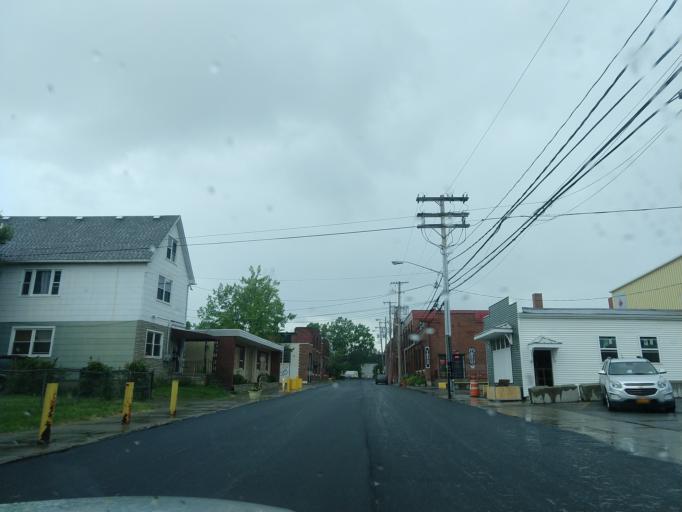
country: US
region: New York
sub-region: Erie County
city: Kenmore
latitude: 42.9422
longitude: -78.8788
